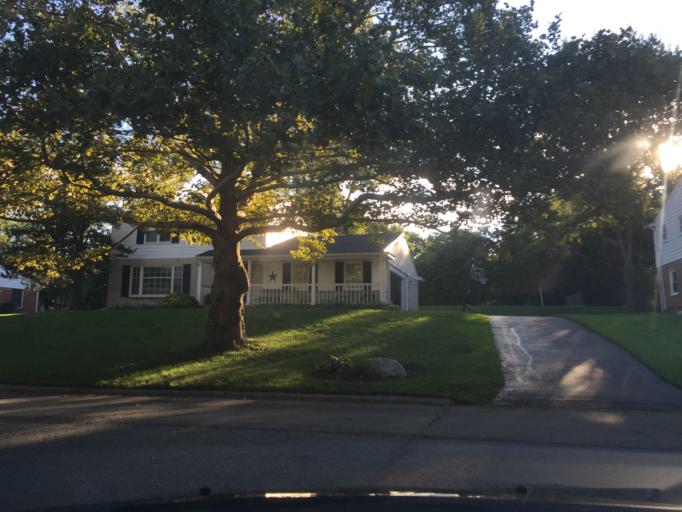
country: US
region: Michigan
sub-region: Oakland County
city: Bloomfield Hills
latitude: 42.6014
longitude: -83.2793
